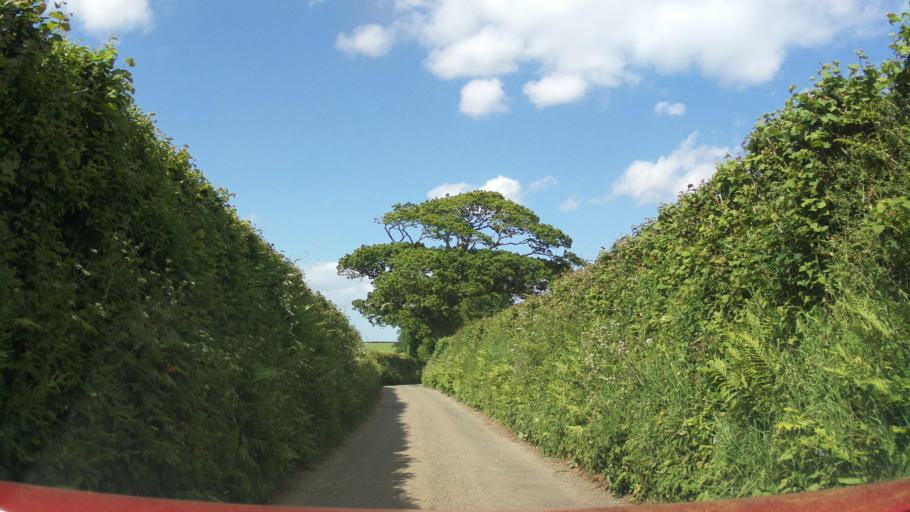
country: GB
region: England
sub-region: Devon
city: Totnes
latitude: 50.4139
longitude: -3.6992
